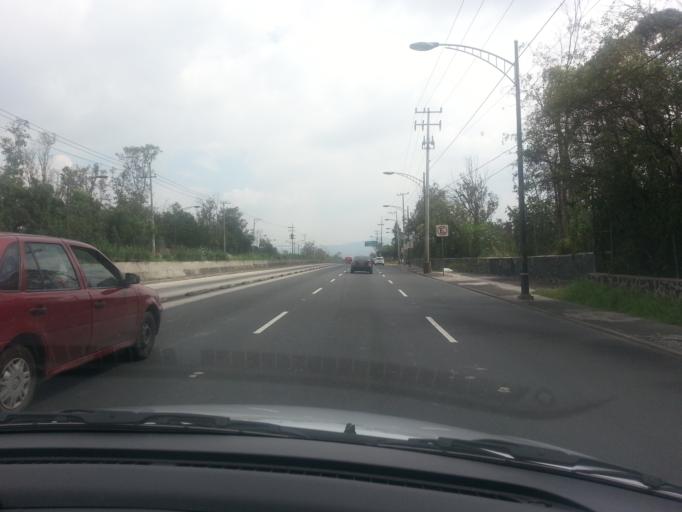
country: MX
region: Mexico City
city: Magdalena Contreras
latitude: 19.3204
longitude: -99.1882
